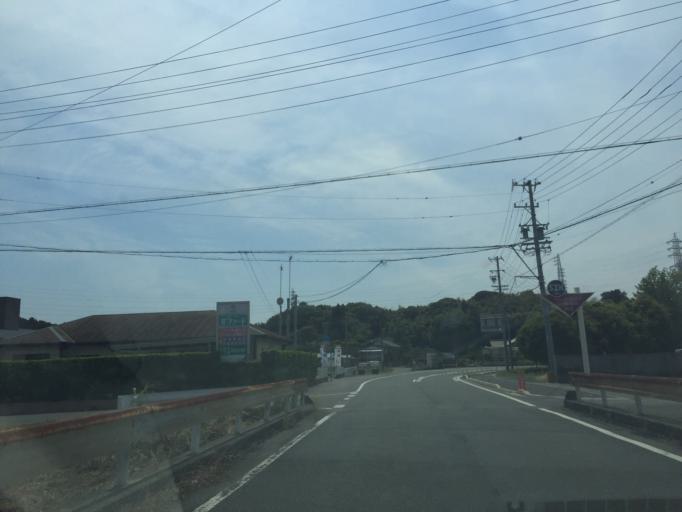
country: JP
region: Shizuoka
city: Kakegawa
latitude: 34.7812
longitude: 137.9667
